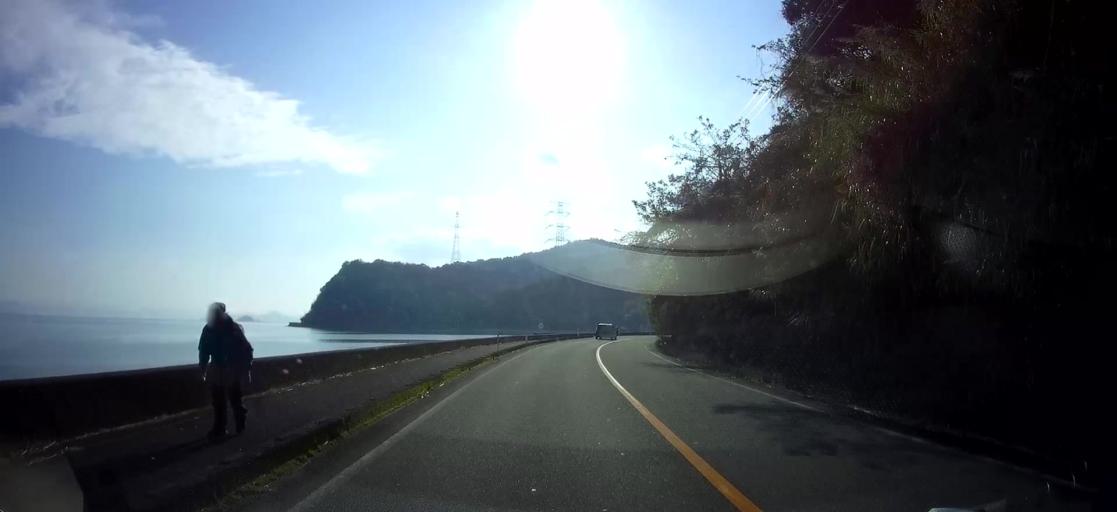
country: JP
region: Kumamoto
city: Yatsushiro
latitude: 32.5127
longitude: 130.4539
